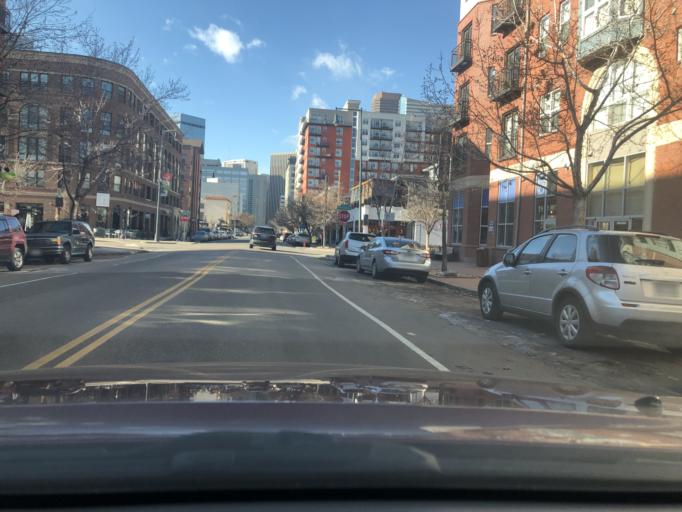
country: US
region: Colorado
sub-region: Denver County
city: Denver
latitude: 39.7462
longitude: -104.9805
